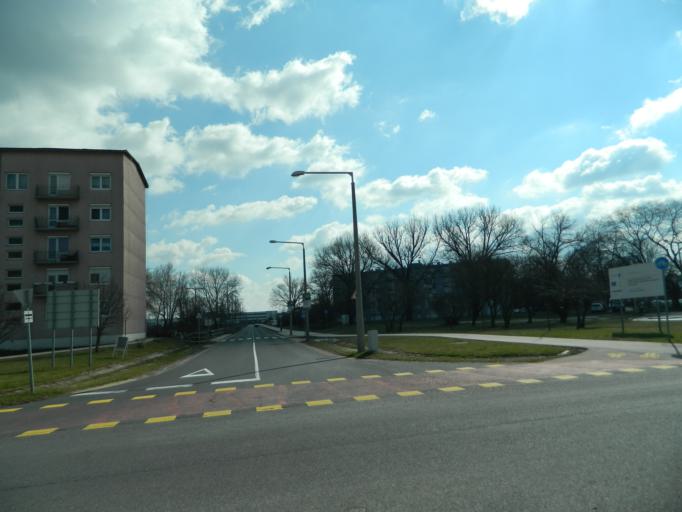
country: HU
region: Fejer
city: Szekesfehervar
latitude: 47.1448
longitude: 18.4083
